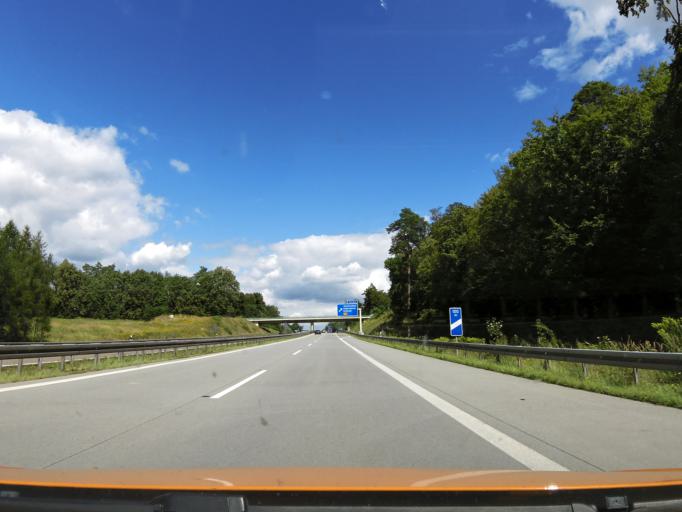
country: DE
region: Brandenburg
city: Althuttendorf
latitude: 52.9504
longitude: 13.8048
